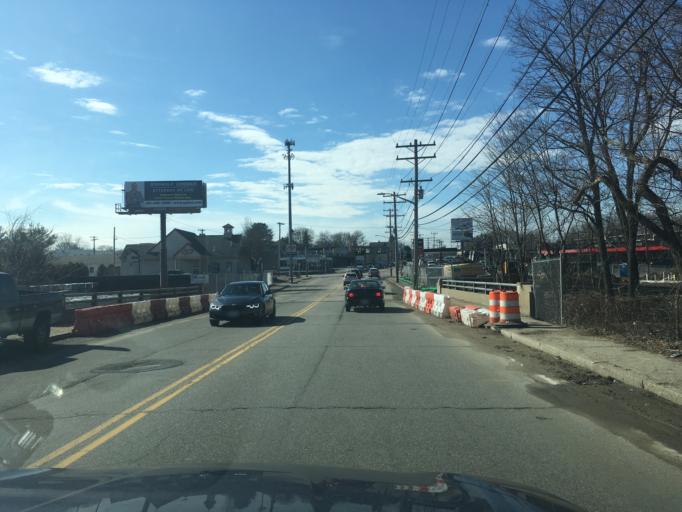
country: US
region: Rhode Island
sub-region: Providence County
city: Cranston
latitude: 41.7844
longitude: -71.4557
